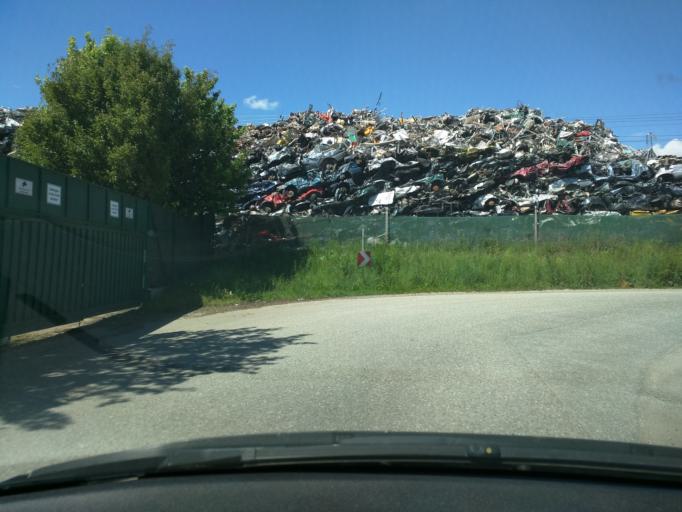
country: AT
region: Lower Austria
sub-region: Politischer Bezirk Amstetten
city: Amstetten
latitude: 48.1222
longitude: 14.9107
